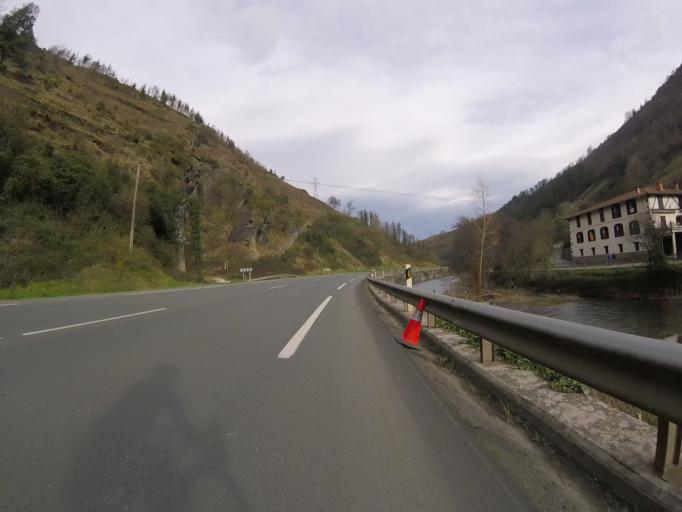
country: ES
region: Basque Country
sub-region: Provincia de Guipuzcoa
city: Azpeitia
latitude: 43.1937
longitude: -2.2592
